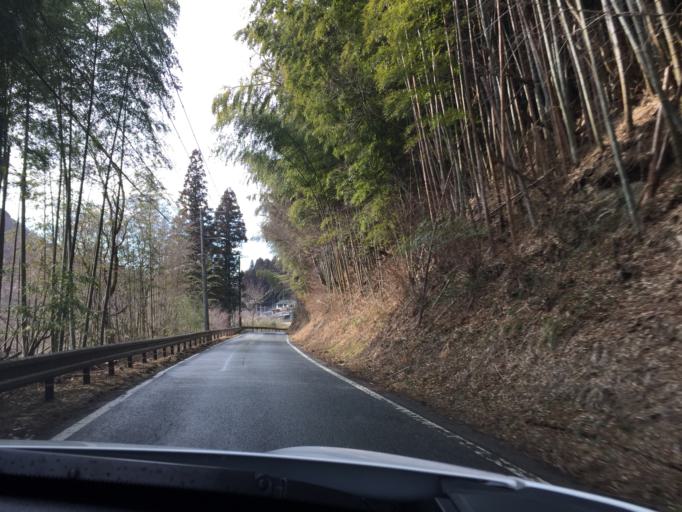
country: JP
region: Fukushima
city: Iwaki
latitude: 37.2087
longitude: 140.7448
